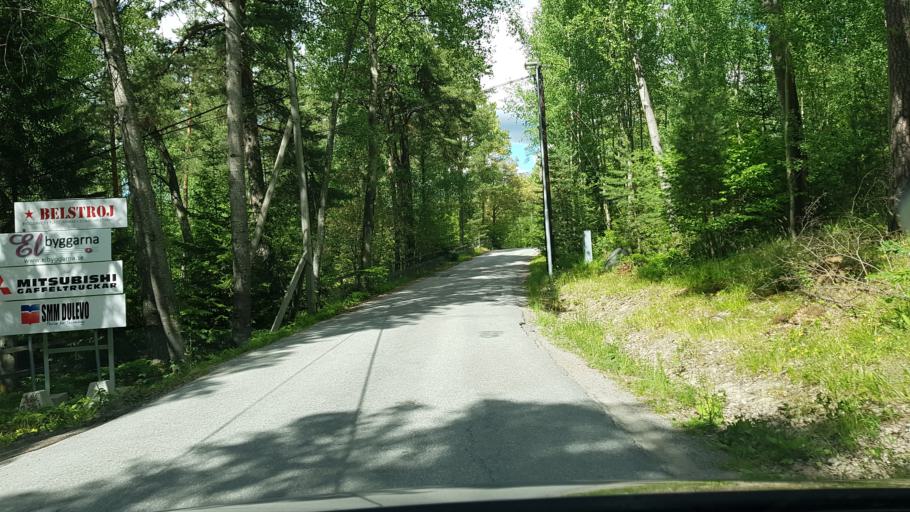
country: SE
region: Stockholm
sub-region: Upplands-Bro Kommun
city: Kungsaengen
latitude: 59.4818
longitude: 17.7997
